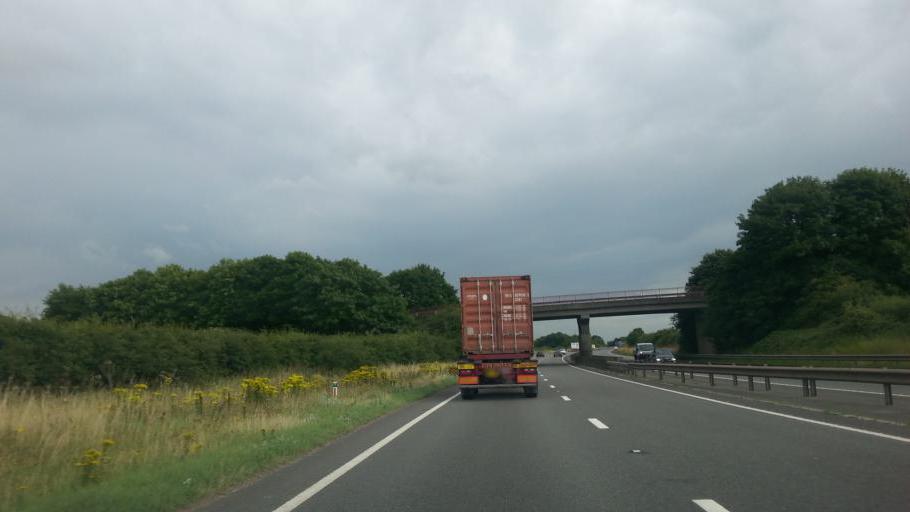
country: GB
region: England
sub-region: Nottinghamshire
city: Newark on Trent
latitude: 53.0649
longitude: -0.7652
